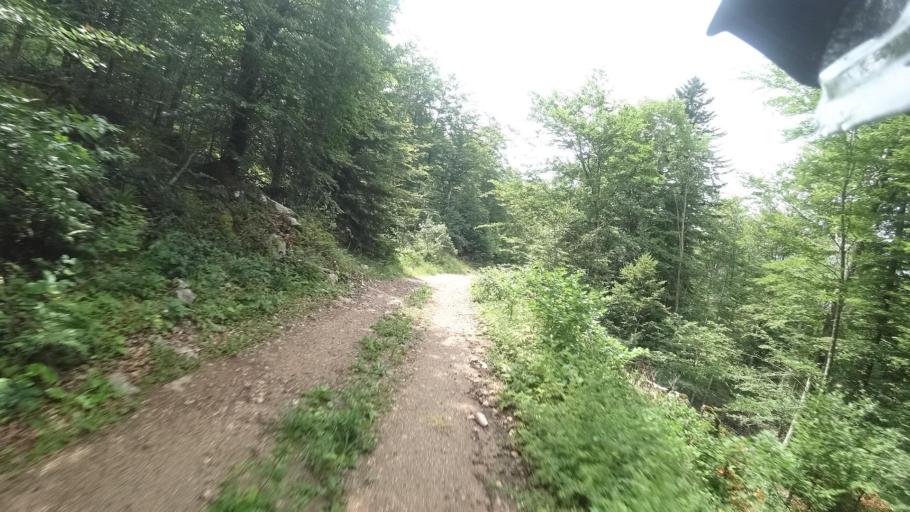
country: BA
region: Federation of Bosnia and Herzegovina
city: Bihac
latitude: 44.6276
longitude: 15.7976
